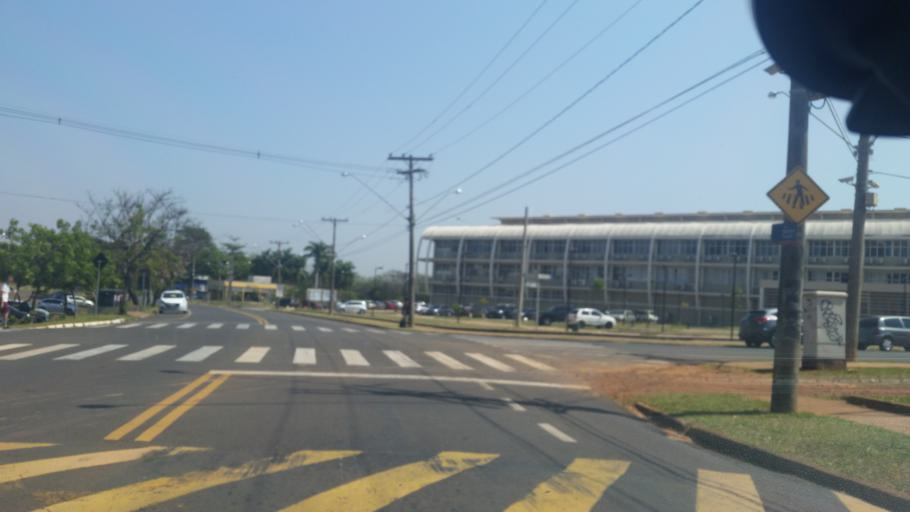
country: BR
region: Sao Paulo
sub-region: Campinas
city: Campinas
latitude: -22.8141
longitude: -47.0681
